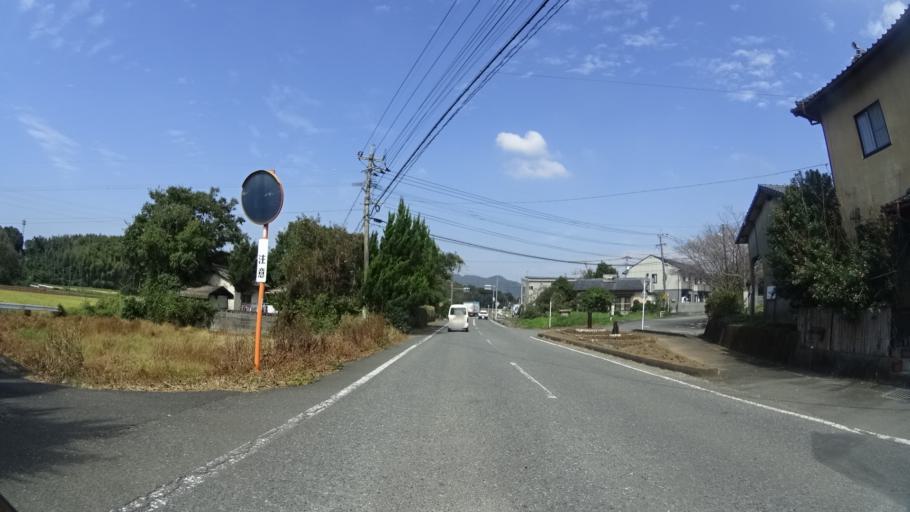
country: JP
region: Kumamoto
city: Matsubase
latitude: 32.6515
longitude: 130.7162
